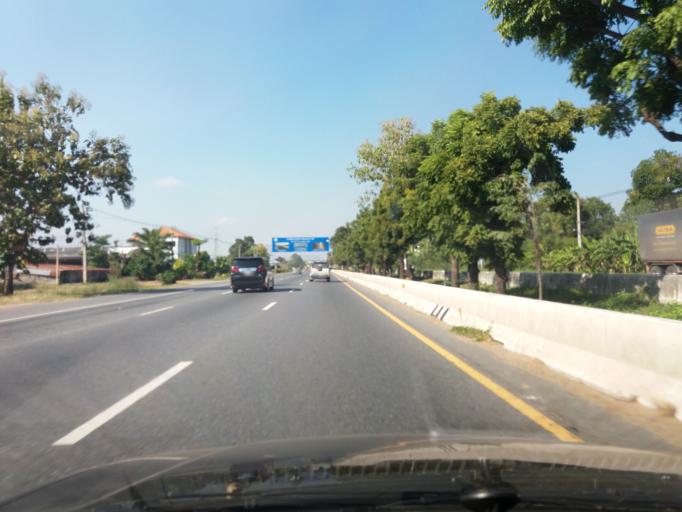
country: TH
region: Nakhon Sawan
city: Krok Phra
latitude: 15.5997
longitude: 100.1225
